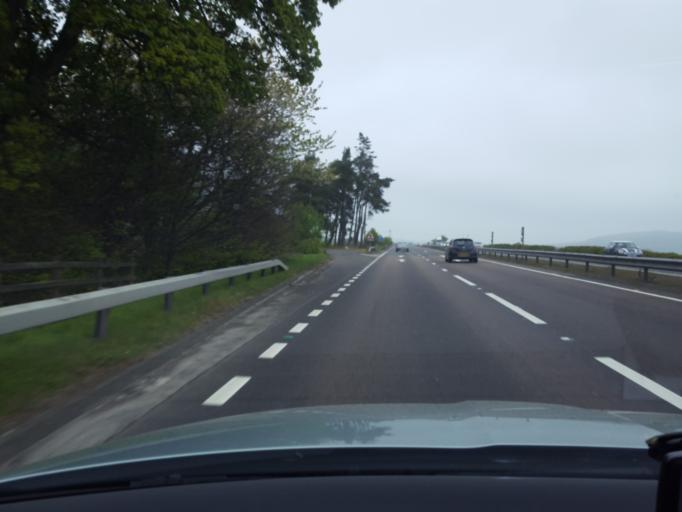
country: GB
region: Scotland
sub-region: Angus
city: Forfar
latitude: 56.5613
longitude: -2.9223
